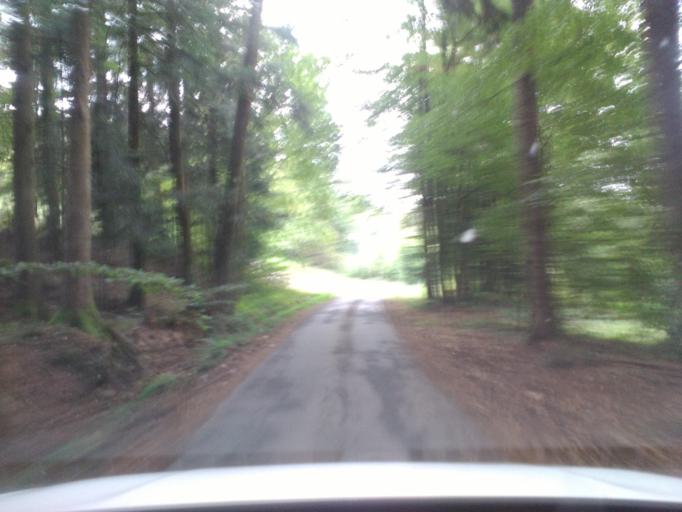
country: FR
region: Lorraine
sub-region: Departement des Vosges
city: Senones
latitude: 48.4199
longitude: 7.0714
